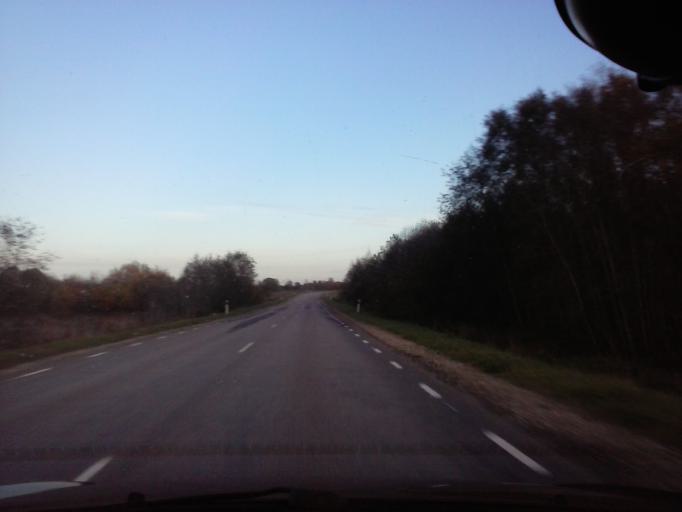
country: EE
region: Harju
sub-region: Nissi vald
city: Turba
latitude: 58.9170
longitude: 24.1830
